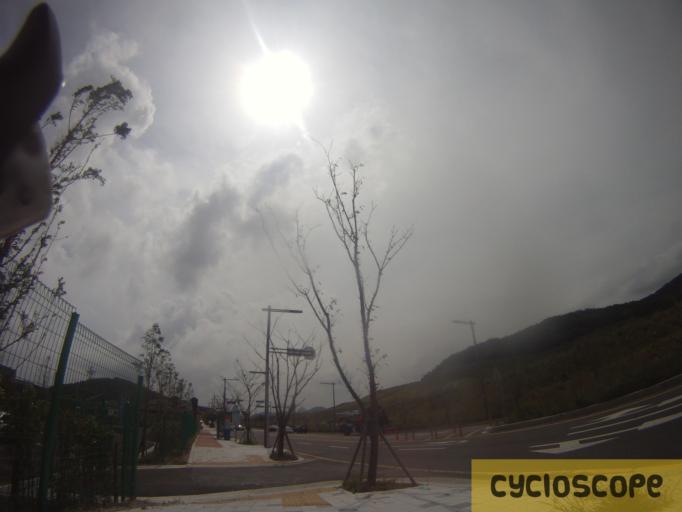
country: KR
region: Busan
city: Kijang
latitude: 35.1955
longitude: 129.2217
